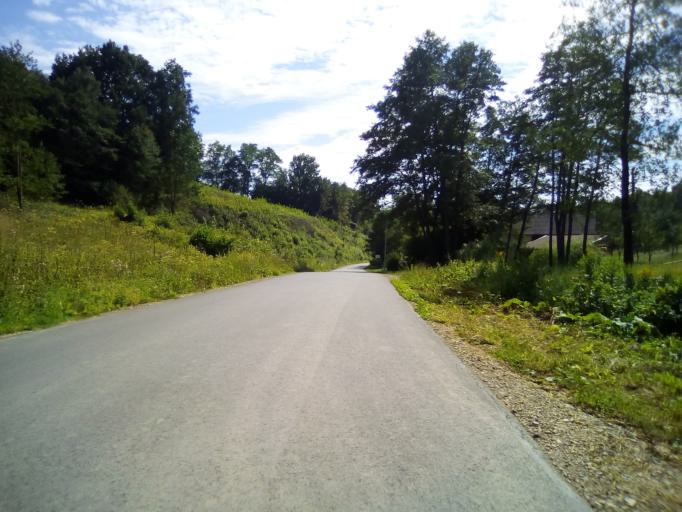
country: PL
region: Subcarpathian Voivodeship
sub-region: Powiat strzyzowski
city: Konieczkowa
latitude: 49.8174
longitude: 21.9240
